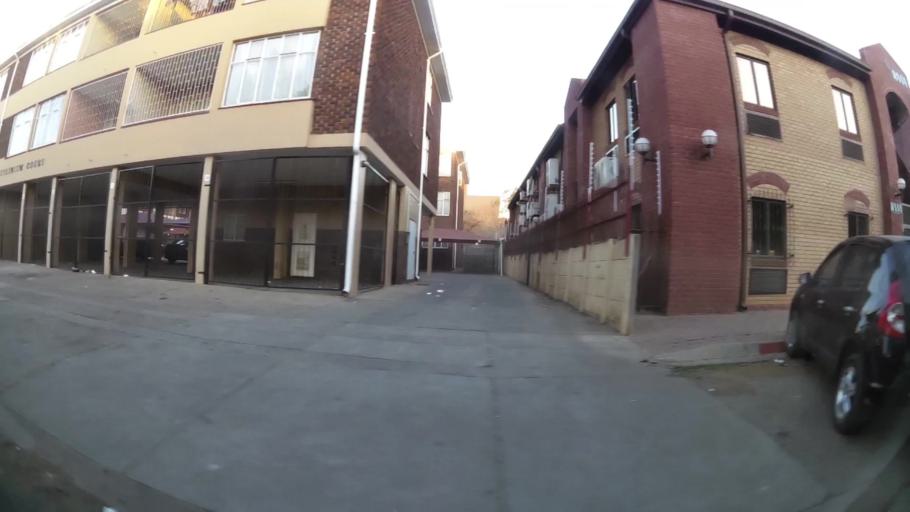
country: ZA
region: North-West
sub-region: Bojanala Platinum District Municipality
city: Rustenburg
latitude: -25.6706
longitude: 27.2392
